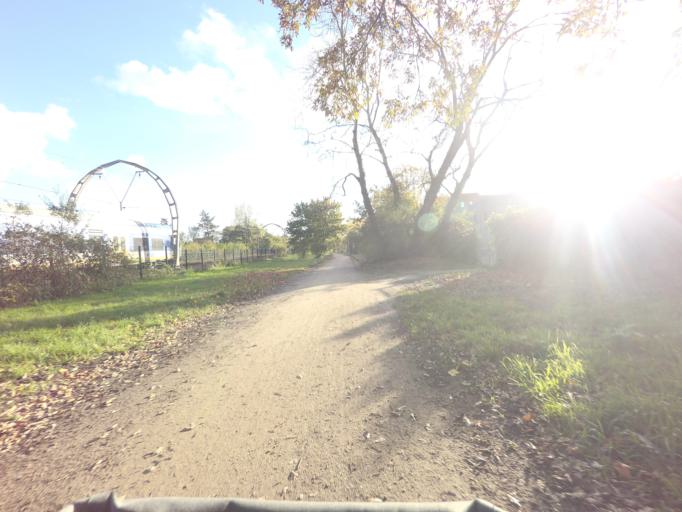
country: NL
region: North Holland
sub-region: Gemeente Hilversum
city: Hilversum
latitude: 52.2143
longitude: 5.1868
